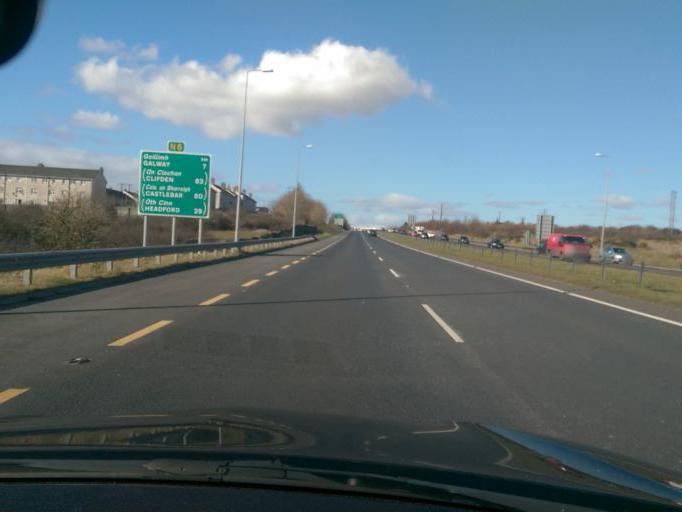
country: IE
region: Connaught
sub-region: County Galway
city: Oranmore
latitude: 53.2863
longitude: -8.9804
